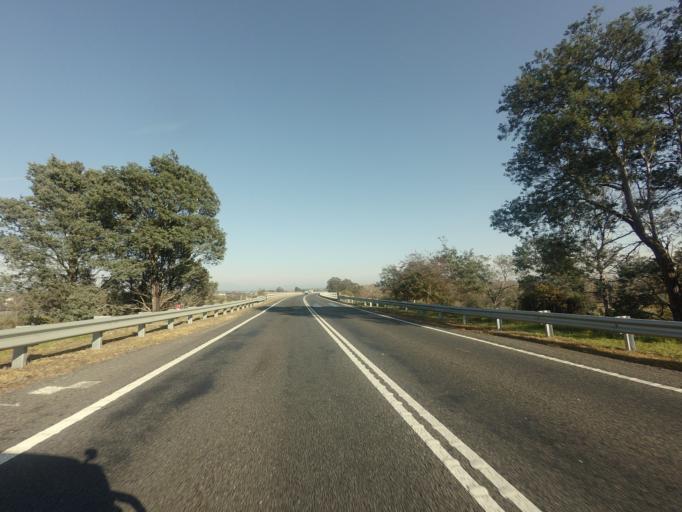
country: AU
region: Tasmania
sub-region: Northern Midlands
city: Longford
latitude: -41.5844
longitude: 147.1280
